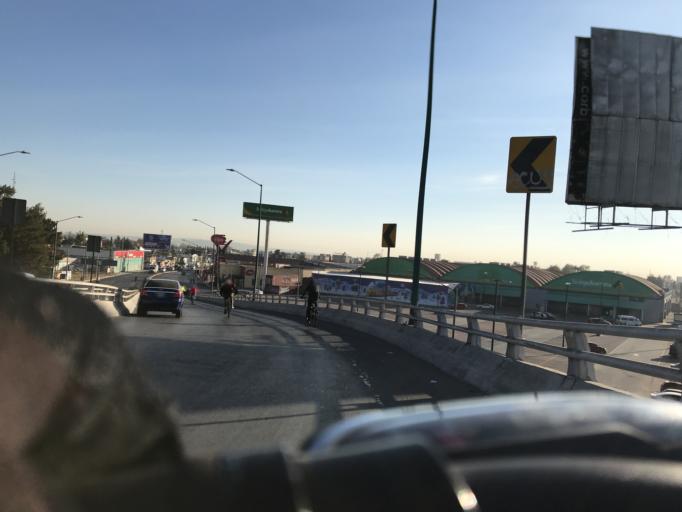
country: MX
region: Mexico
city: Cuautitlan
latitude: 19.6702
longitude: -99.1758
